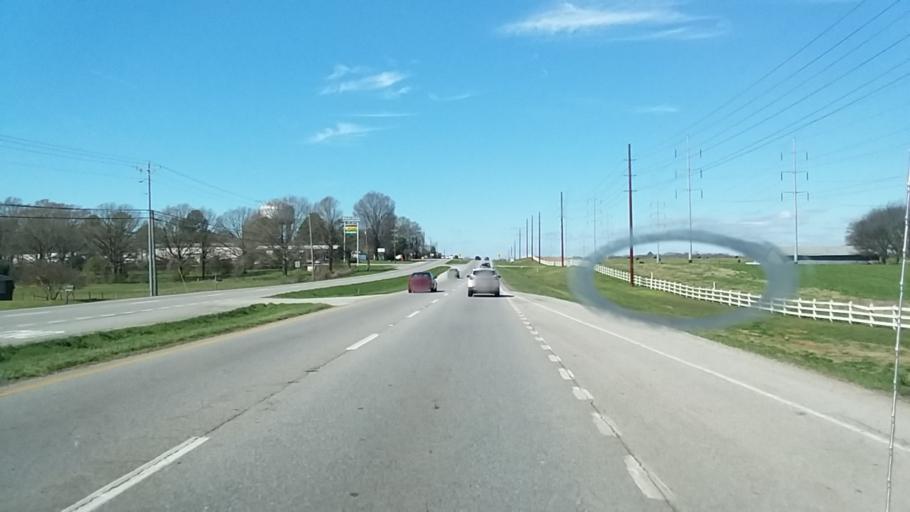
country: US
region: Alabama
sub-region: Morgan County
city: Decatur
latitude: 34.6194
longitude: -87.0228
